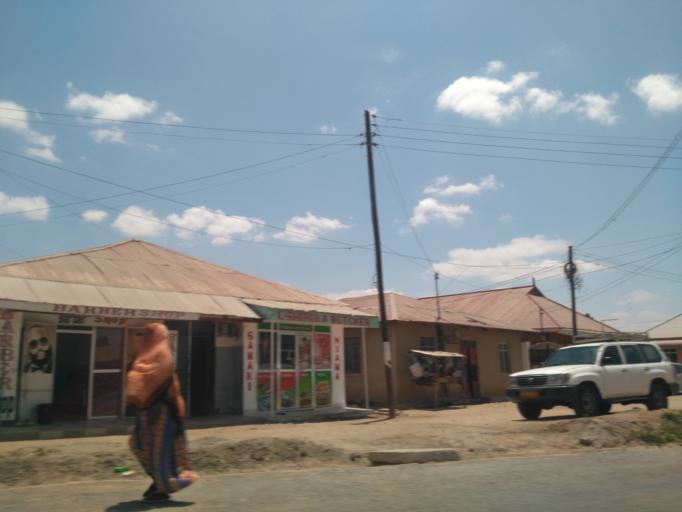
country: TZ
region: Dodoma
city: Dodoma
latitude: -6.1724
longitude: 35.7491
